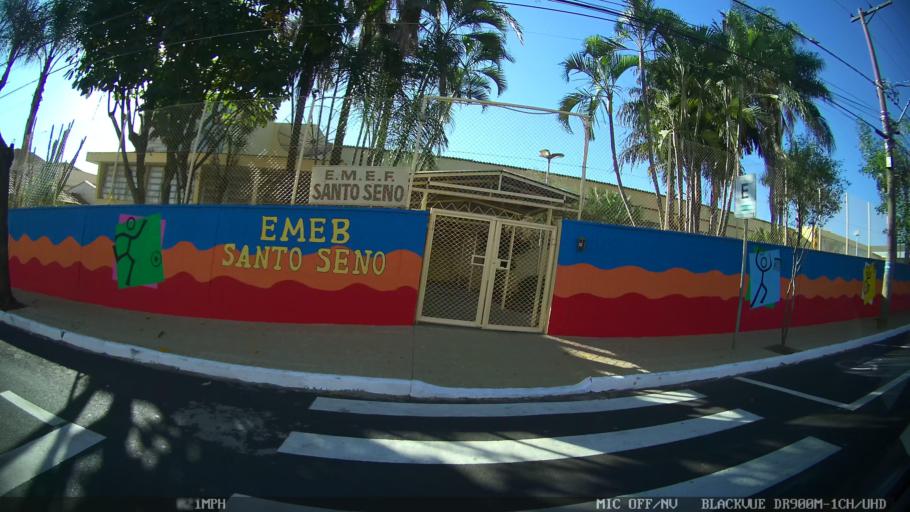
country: BR
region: Sao Paulo
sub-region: Olimpia
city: Olimpia
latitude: -20.7369
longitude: -48.9061
